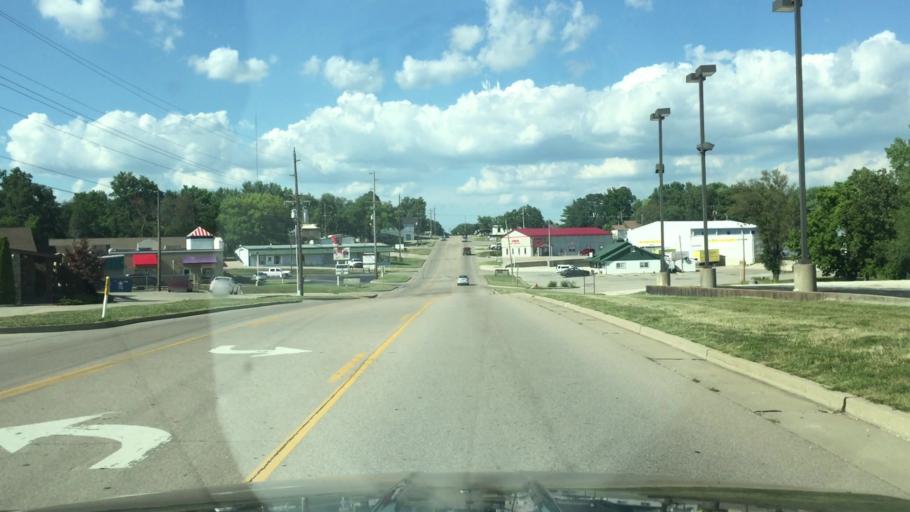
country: US
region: Missouri
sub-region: Miller County
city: Eldon
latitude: 38.3373
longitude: -92.5843
